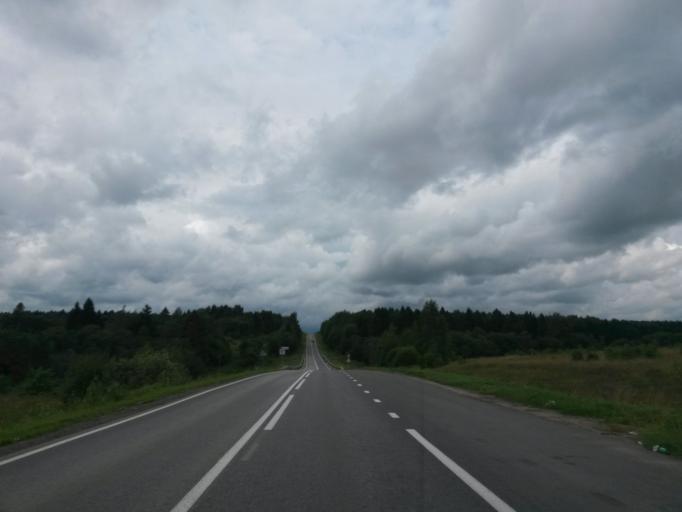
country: RU
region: Jaroslavl
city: Konstantinovskiy
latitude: 57.8134
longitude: 39.7233
